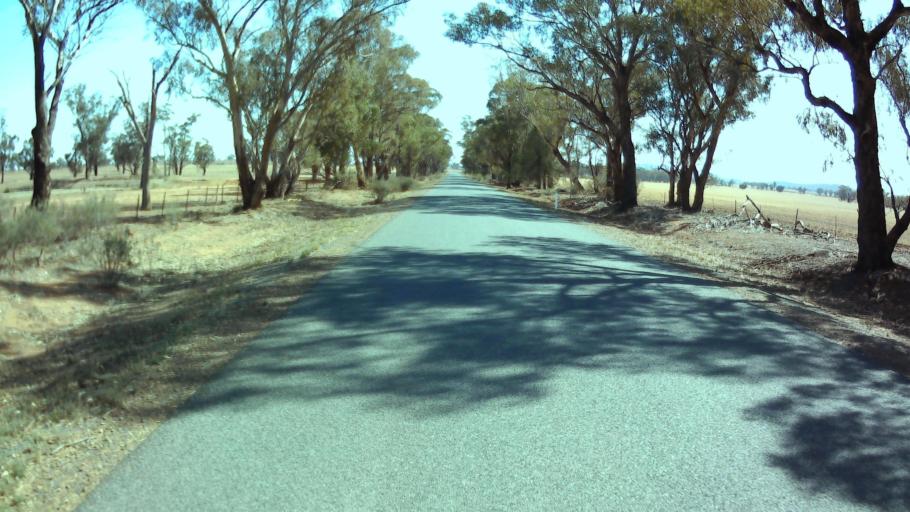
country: AU
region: New South Wales
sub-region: Weddin
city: Grenfell
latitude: -33.7420
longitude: 147.8804
